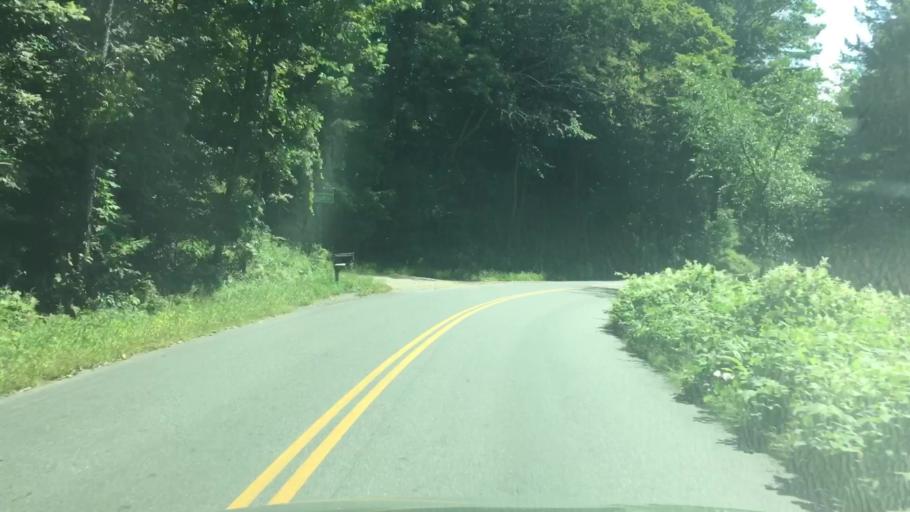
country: US
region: Vermont
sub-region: Windham County
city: West Brattleboro
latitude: 42.8052
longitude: -72.6071
